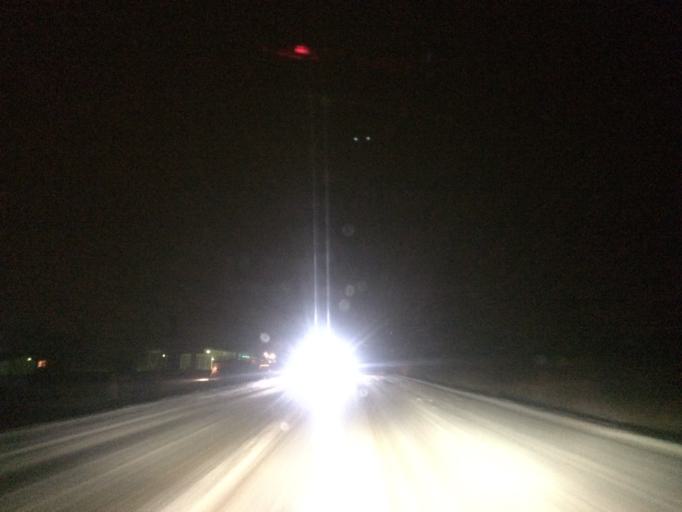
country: RU
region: Tula
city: Kosaya Gora
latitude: 54.1503
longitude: 37.4283
